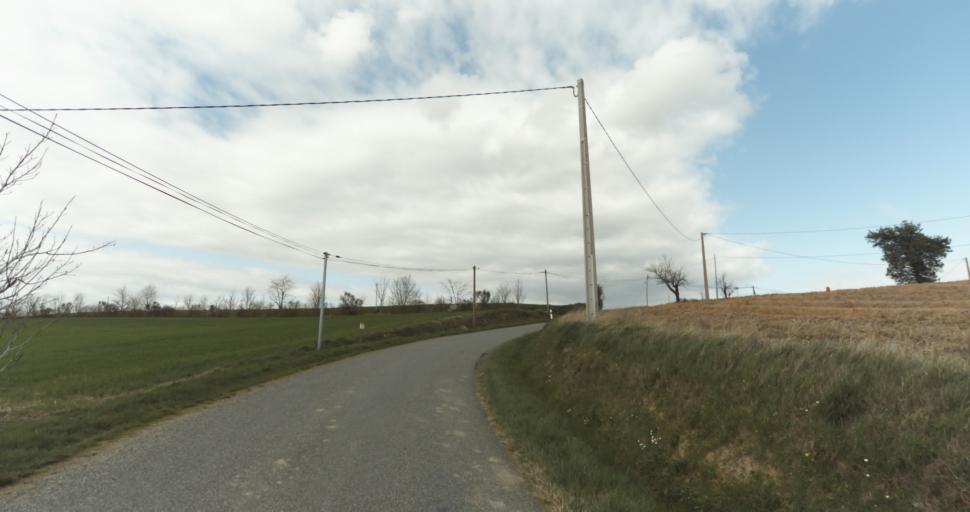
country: FR
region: Midi-Pyrenees
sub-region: Departement de la Haute-Garonne
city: Auterive
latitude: 43.3818
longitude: 1.4895
